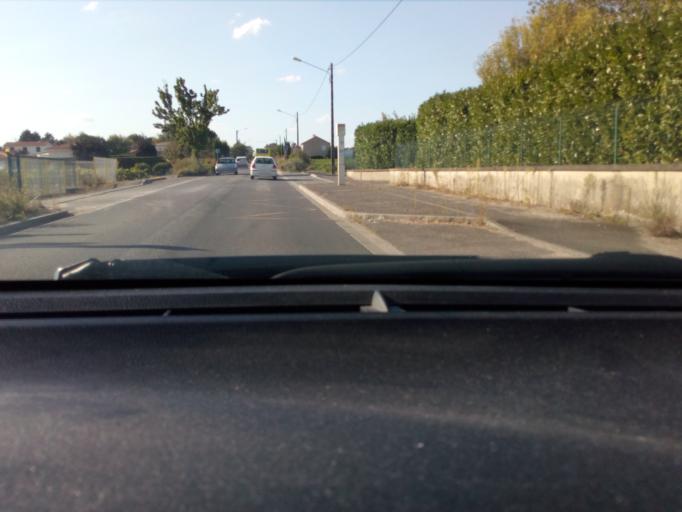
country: FR
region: Poitou-Charentes
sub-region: Departement de la Charente
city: Saint-Yrieix-sur-Charente
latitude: 45.6798
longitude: 0.1177
